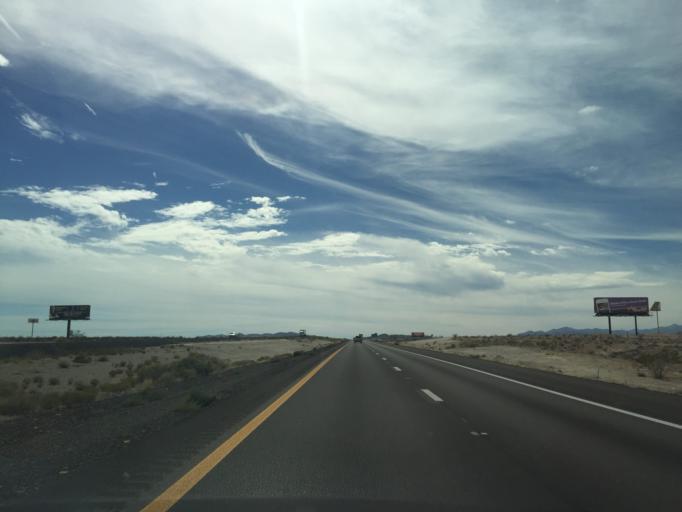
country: US
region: Nevada
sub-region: Clark County
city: Moapa Town
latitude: 36.5177
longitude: -114.7403
